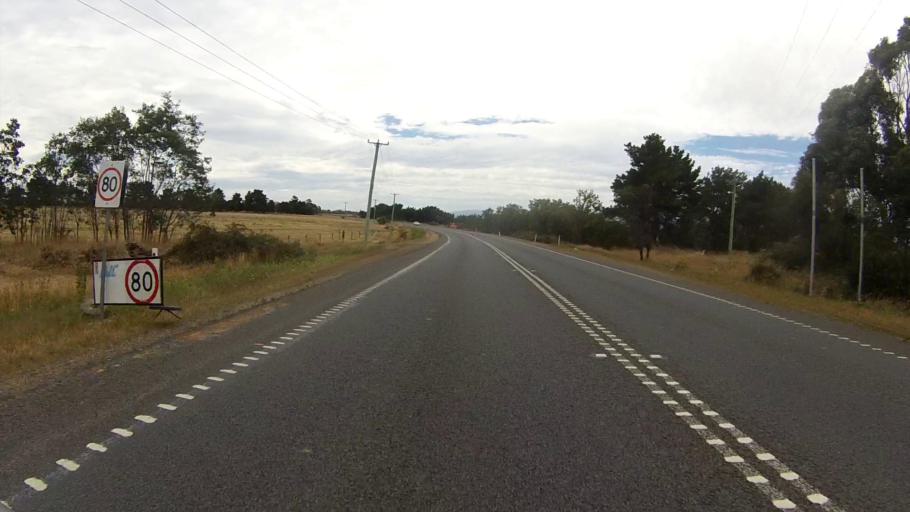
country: AU
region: Tasmania
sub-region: Northern Midlands
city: Evandale
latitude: -41.6201
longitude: 147.2261
